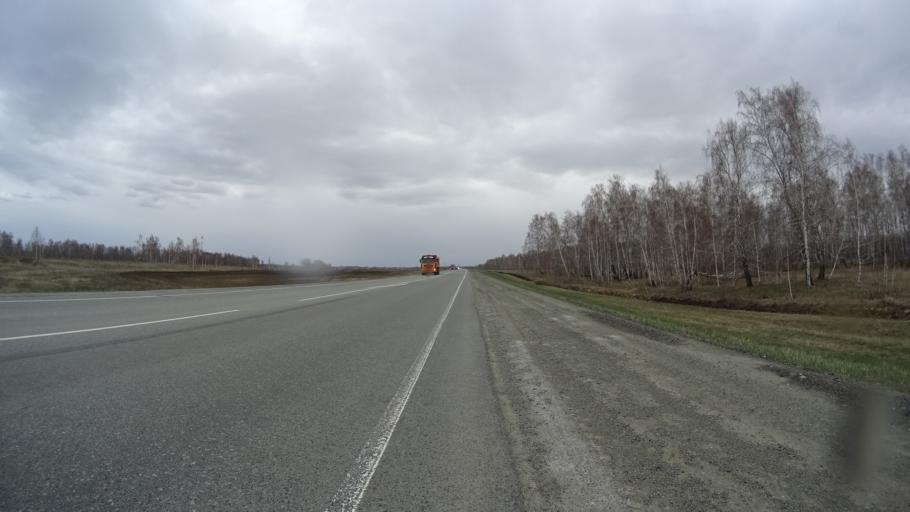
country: RU
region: Chelyabinsk
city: Krasnogorskiy
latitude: 54.6921
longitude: 61.2490
